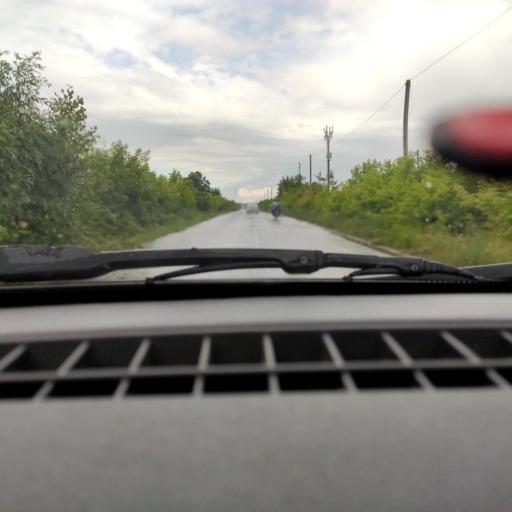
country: RU
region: Bashkortostan
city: Kabakovo
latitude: 54.5742
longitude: 56.2750
